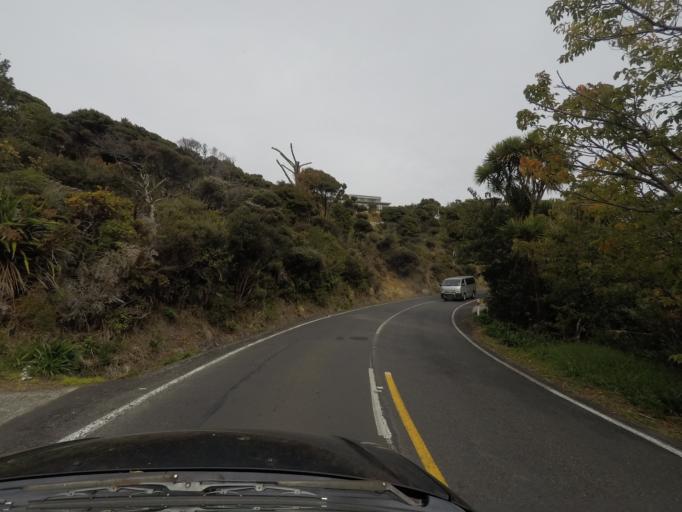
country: NZ
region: Auckland
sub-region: Auckland
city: Muriwai Beach
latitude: -36.9617
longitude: 174.4752
